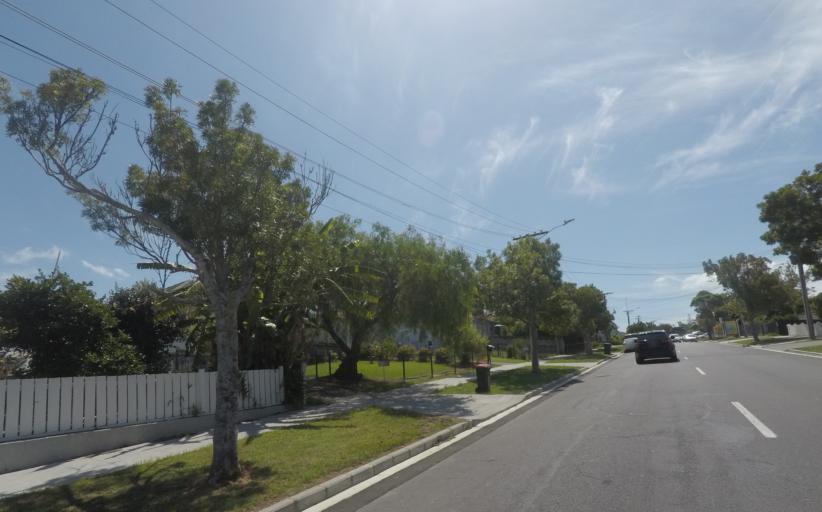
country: NZ
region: Auckland
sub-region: Auckland
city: Tamaki
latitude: -36.8712
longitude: 174.8516
